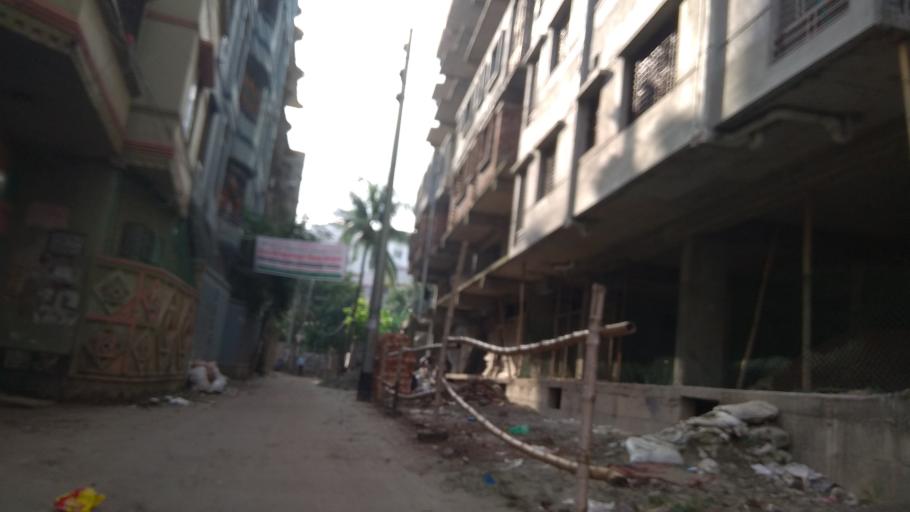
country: BD
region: Dhaka
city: Azimpur
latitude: 23.7935
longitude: 90.3792
